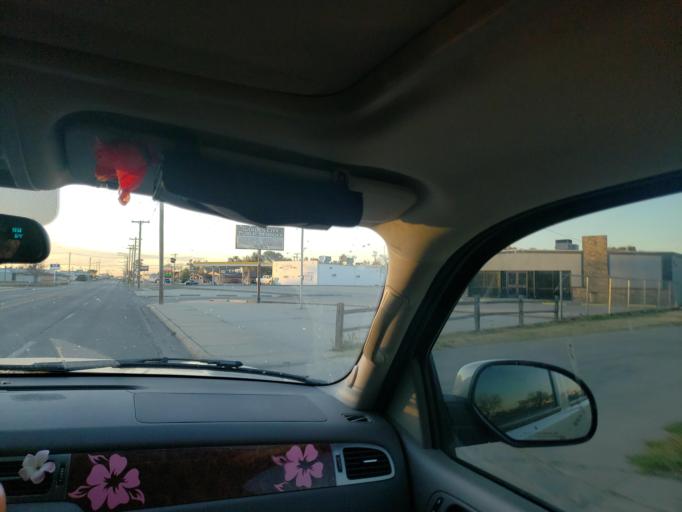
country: US
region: Kansas
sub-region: Finney County
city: Garden City
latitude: 37.9761
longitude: -100.8857
